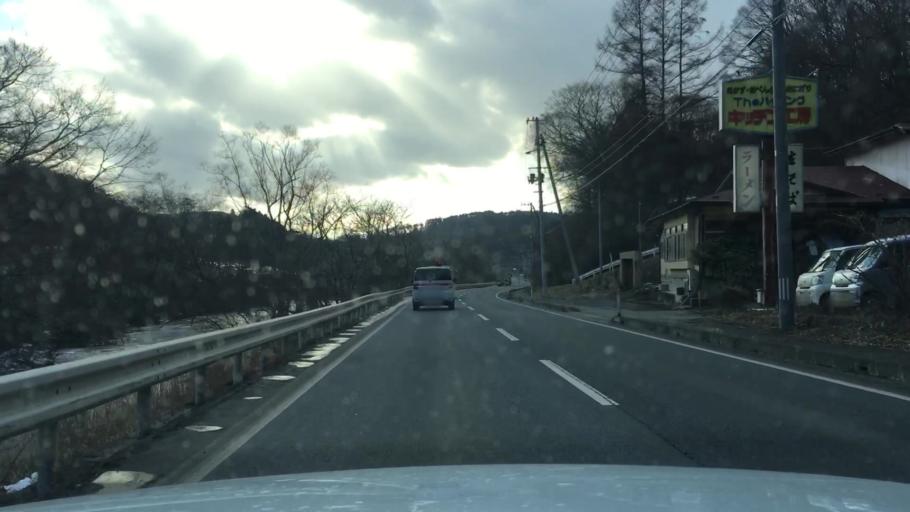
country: JP
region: Iwate
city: Morioka-shi
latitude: 39.6761
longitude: 141.2194
